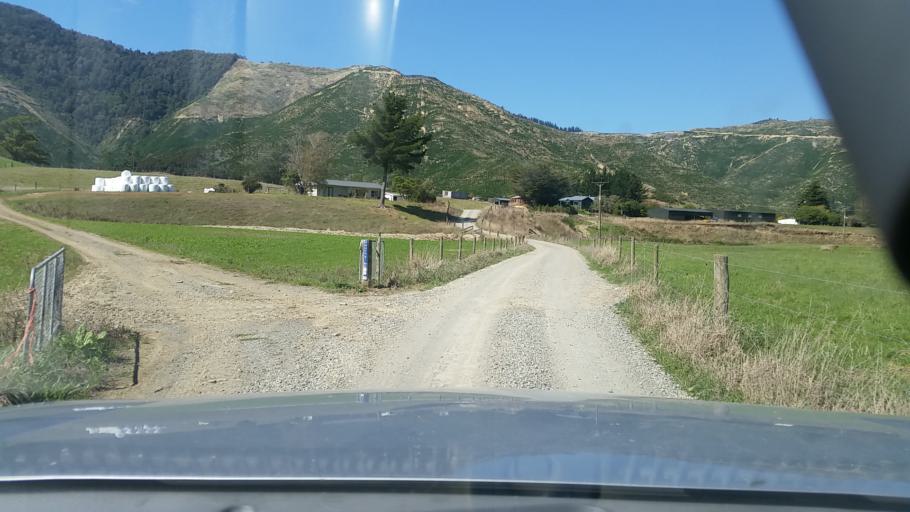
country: NZ
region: Nelson
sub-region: Nelson City
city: Nelson
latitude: -41.2703
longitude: 173.5783
